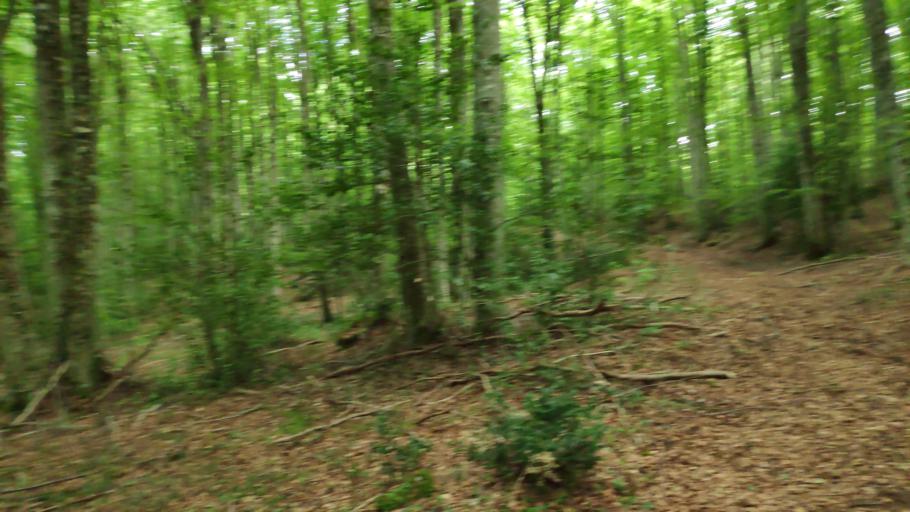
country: IT
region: Calabria
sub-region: Provincia di Vibo-Valentia
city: Mongiana
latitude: 38.5187
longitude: 16.3574
